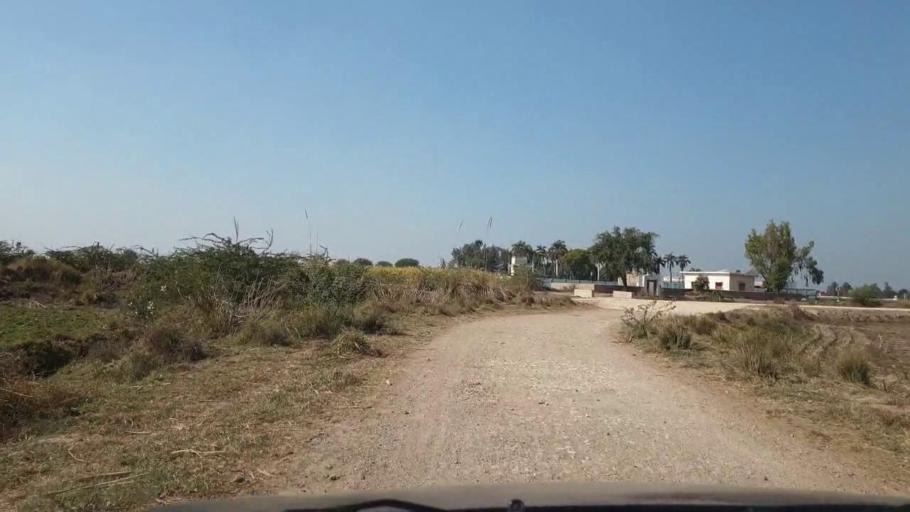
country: PK
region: Sindh
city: Jhol
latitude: 25.9137
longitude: 68.8125
